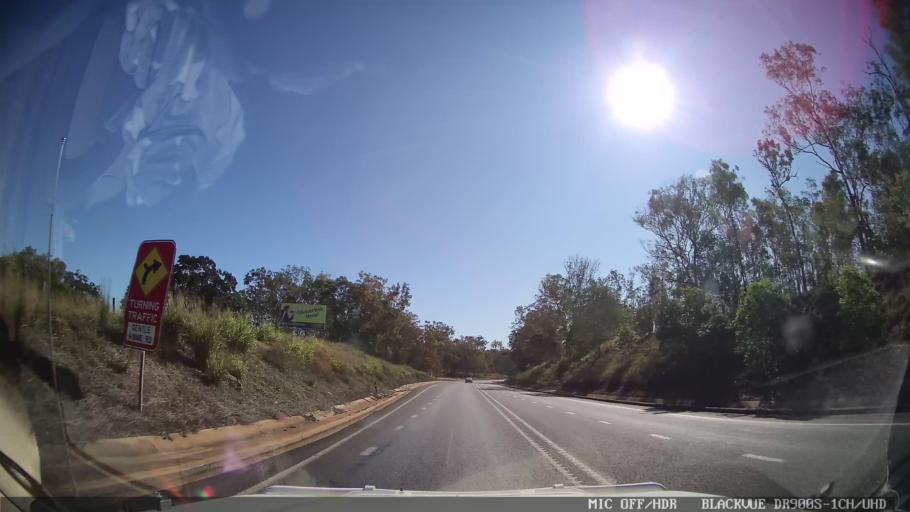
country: AU
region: Queensland
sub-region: Bundaberg
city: Childers
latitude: -25.2331
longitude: 152.2448
